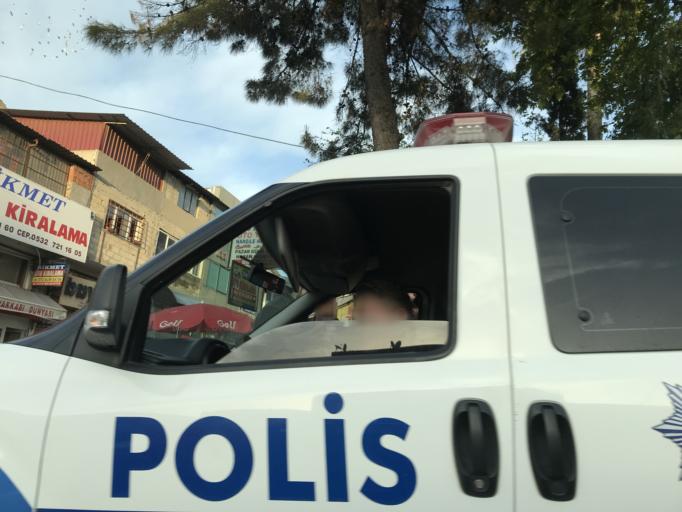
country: TR
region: Hatay
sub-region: Antakya Ilcesi
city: Antakya
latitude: 36.2072
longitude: 36.1648
